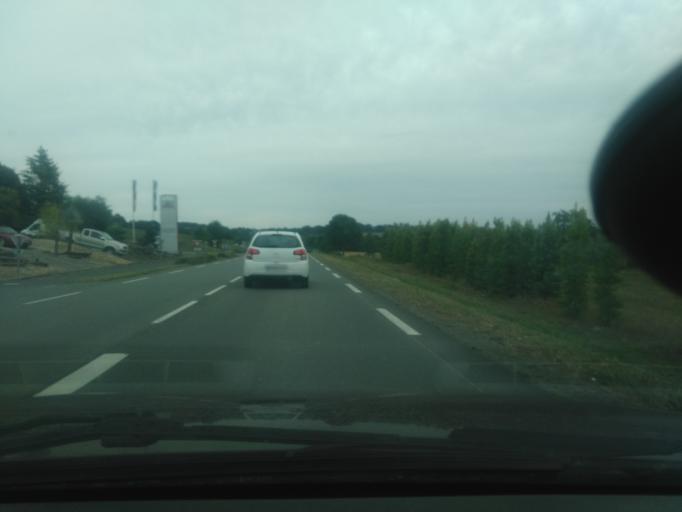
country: FR
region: Pays de la Loire
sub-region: Departement de la Vendee
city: Antigny
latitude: 46.6589
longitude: -0.7812
